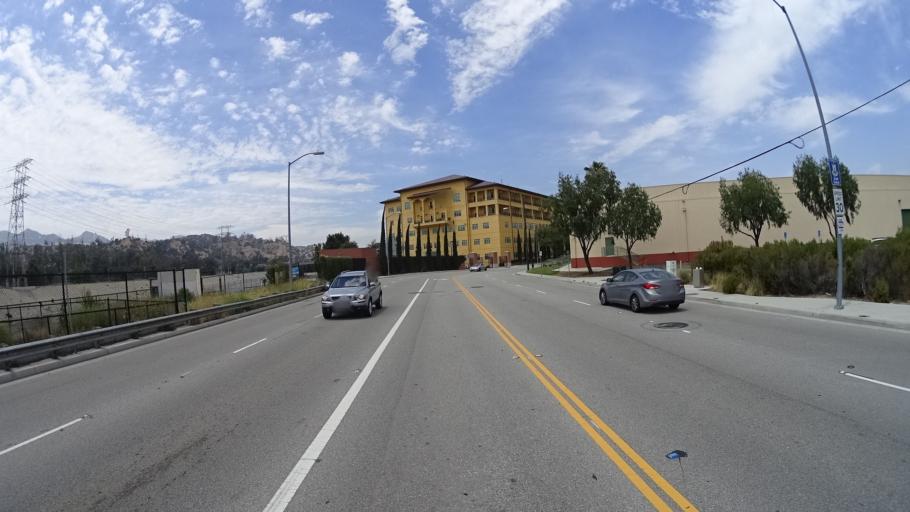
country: US
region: California
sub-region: Los Angeles County
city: North Glendale
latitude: 34.1568
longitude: -118.2826
